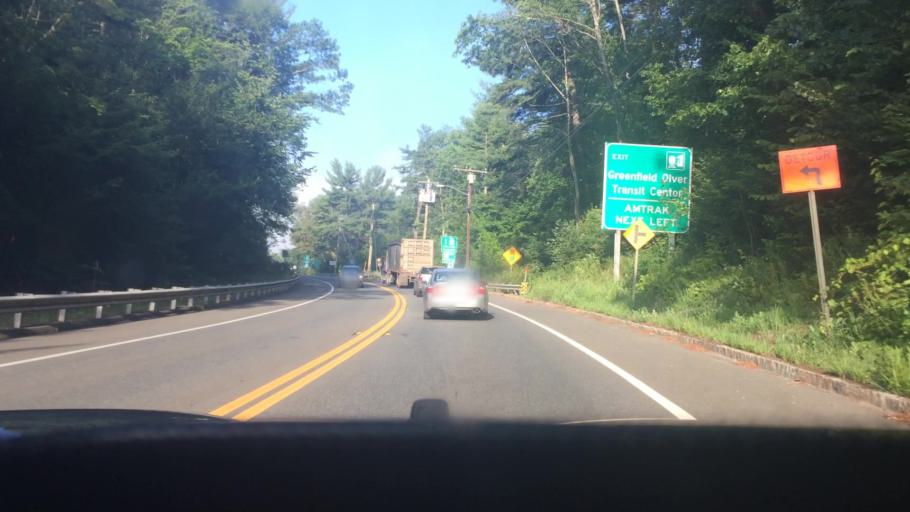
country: US
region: Massachusetts
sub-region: Franklin County
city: Turners Falls
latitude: 42.6167
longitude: -72.5574
